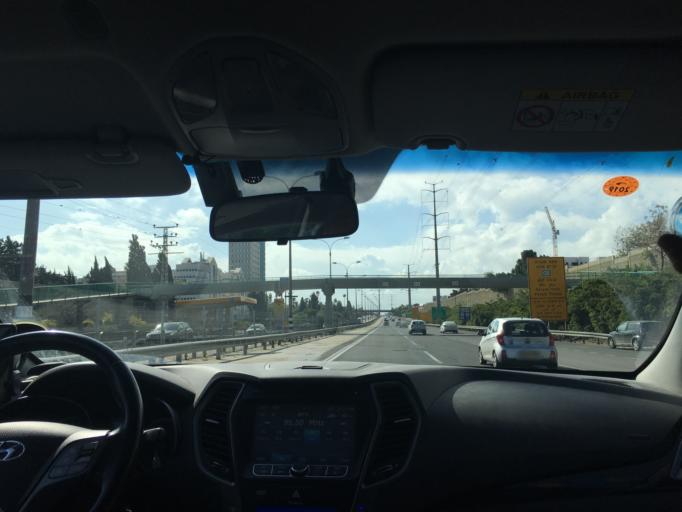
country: IL
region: Tel Aviv
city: Giv`at Shemu'el
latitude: 32.0831
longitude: 34.8453
